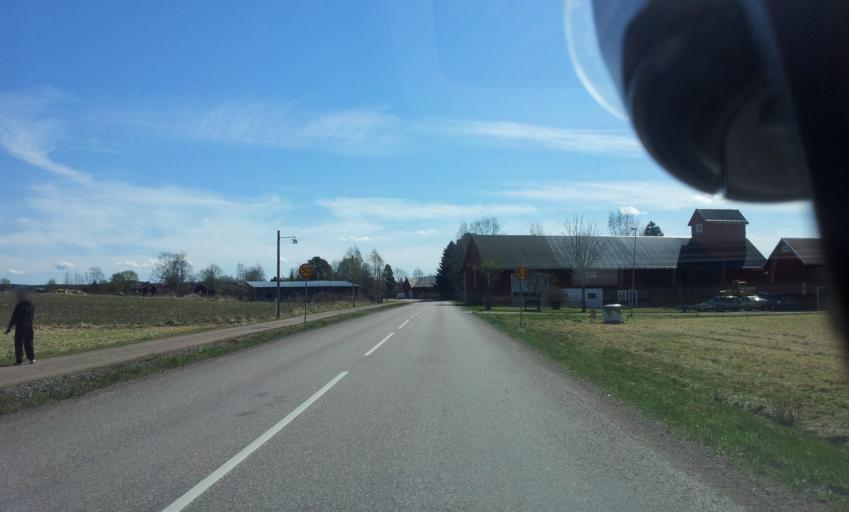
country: SE
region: Dalarna
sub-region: Borlange Kommun
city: Ornas
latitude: 60.4657
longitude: 15.5156
